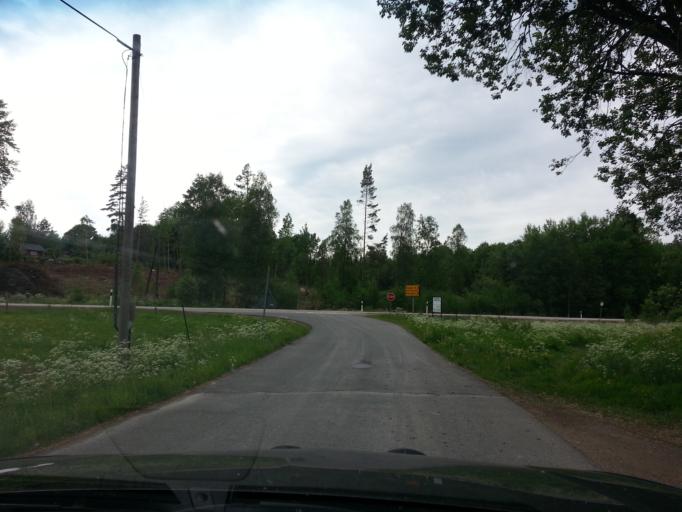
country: SE
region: Joenkoeping
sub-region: Vetlanda Kommun
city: Vetlanda
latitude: 57.2859
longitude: 15.1326
